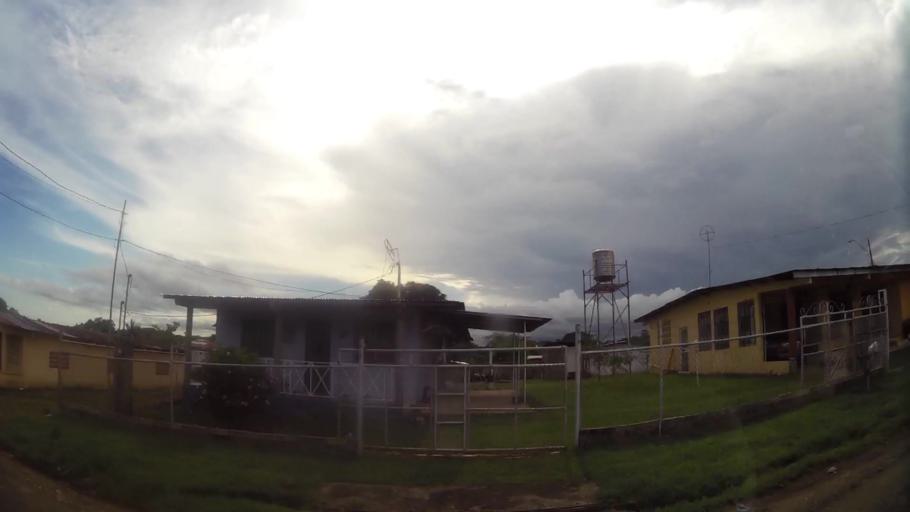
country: PA
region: Panama
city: El Coco
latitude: 8.8774
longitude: -79.8098
